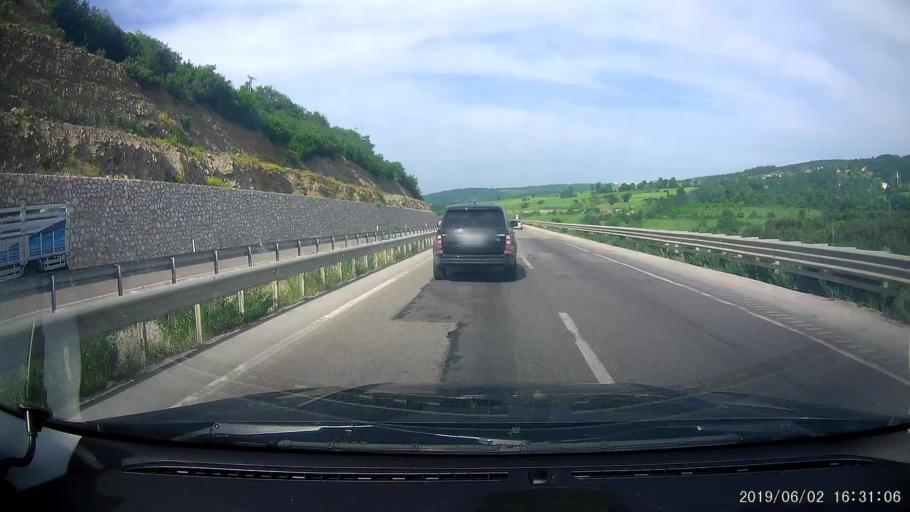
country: TR
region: Samsun
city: Ladik
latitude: 41.0300
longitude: 35.8956
